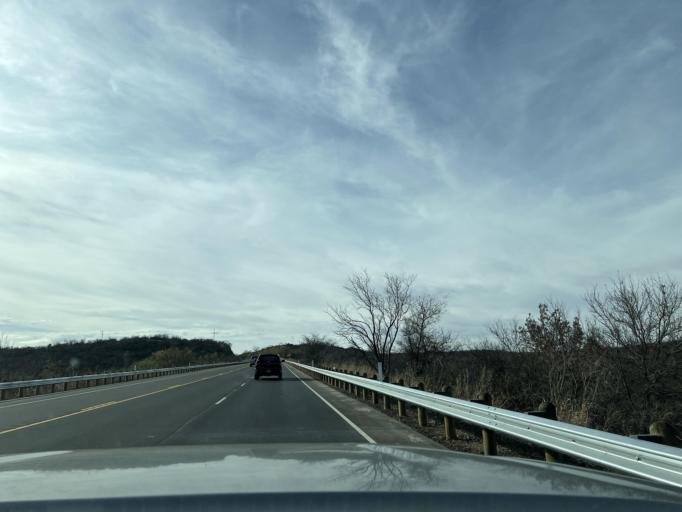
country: US
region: Texas
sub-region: Shackelford County
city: Albany
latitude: 32.7180
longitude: -99.3115
